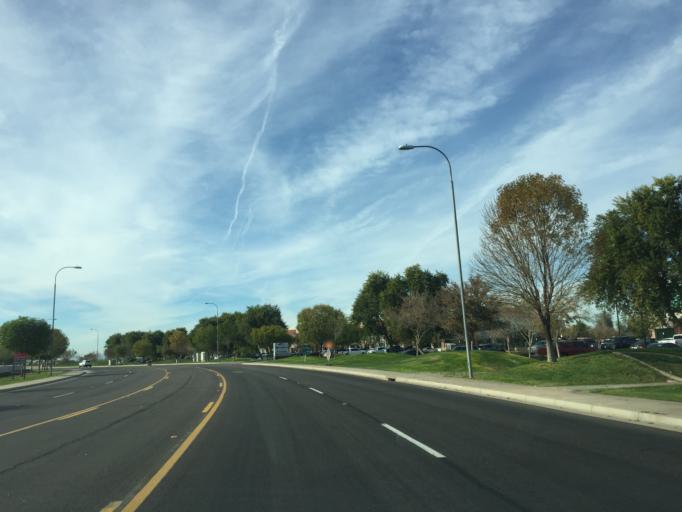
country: US
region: Arizona
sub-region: Maricopa County
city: Chandler
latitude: 33.2806
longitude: -111.8100
